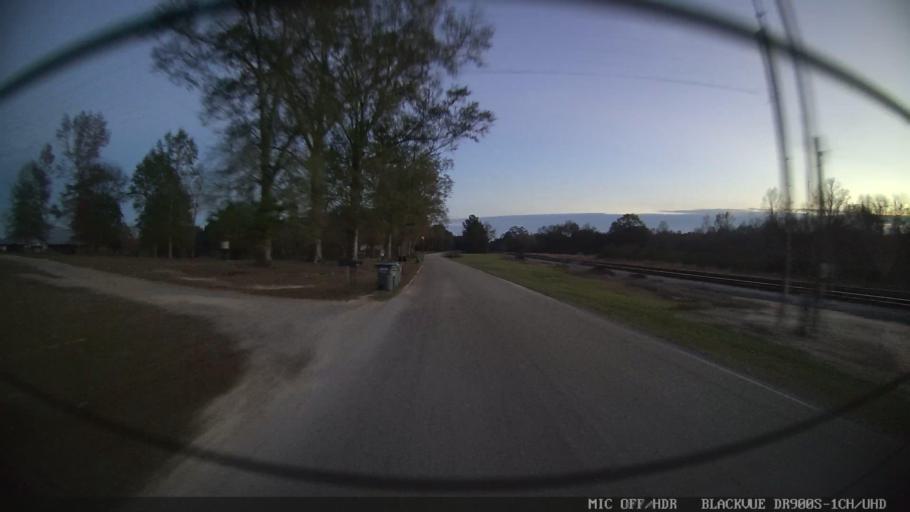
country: US
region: Mississippi
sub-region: Perry County
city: New Augusta
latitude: 31.1619
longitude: -89.2128
